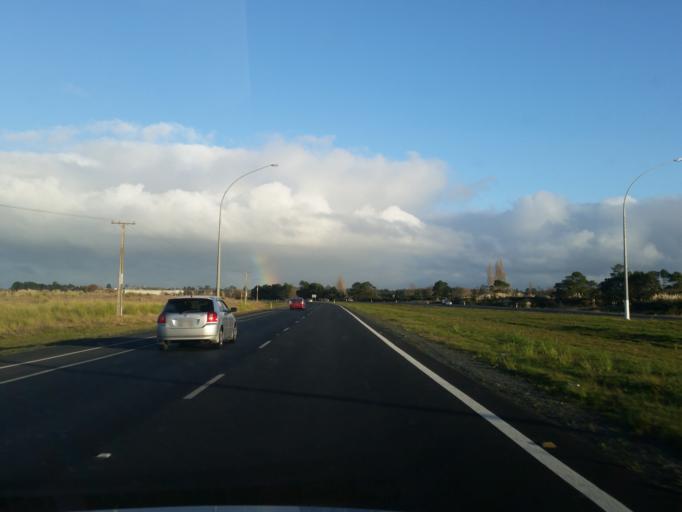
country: NZ
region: Waikato
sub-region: Waikato District
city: Te Kauwhata
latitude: -37.2974
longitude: 175.0602
